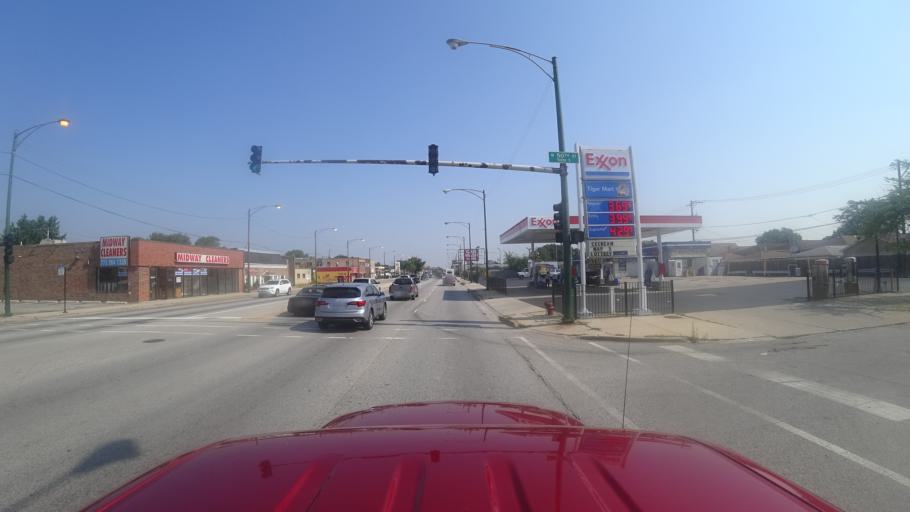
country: US
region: Illinois
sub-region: Cook County
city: Stickney
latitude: 41.8021
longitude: -87.7429
